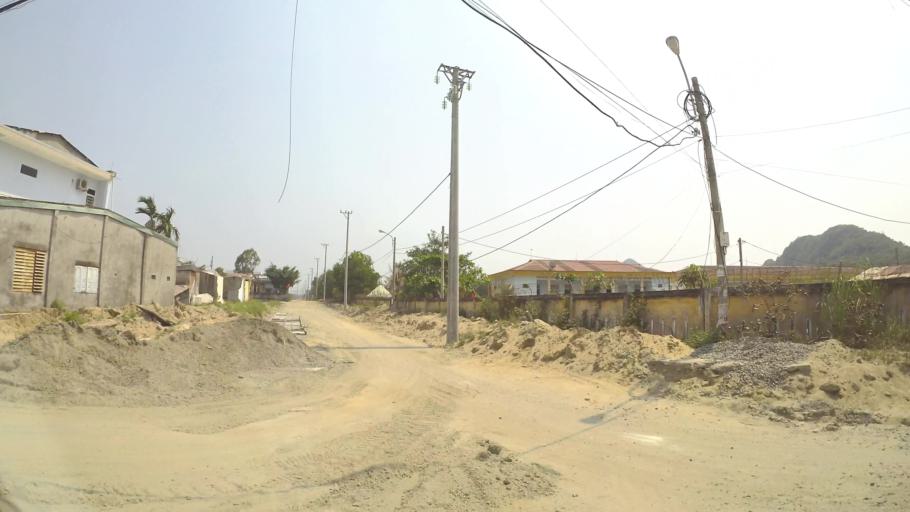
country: VN
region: Da Nang
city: Ngu Hanh Son
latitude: 16.0076
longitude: 108.2532
